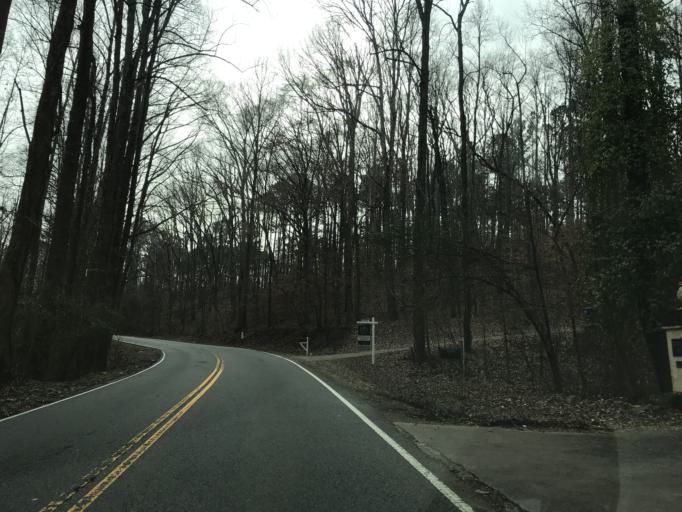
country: US
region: Georgia
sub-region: Fulton County
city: Milton
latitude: 34.1777
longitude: -84.3359
